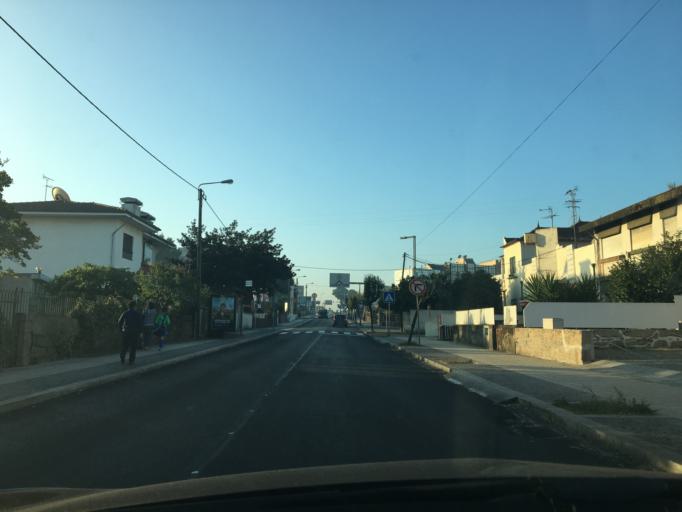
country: PT
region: Porto
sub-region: Maia
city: Anta
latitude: 41.2618
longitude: -8.6162
